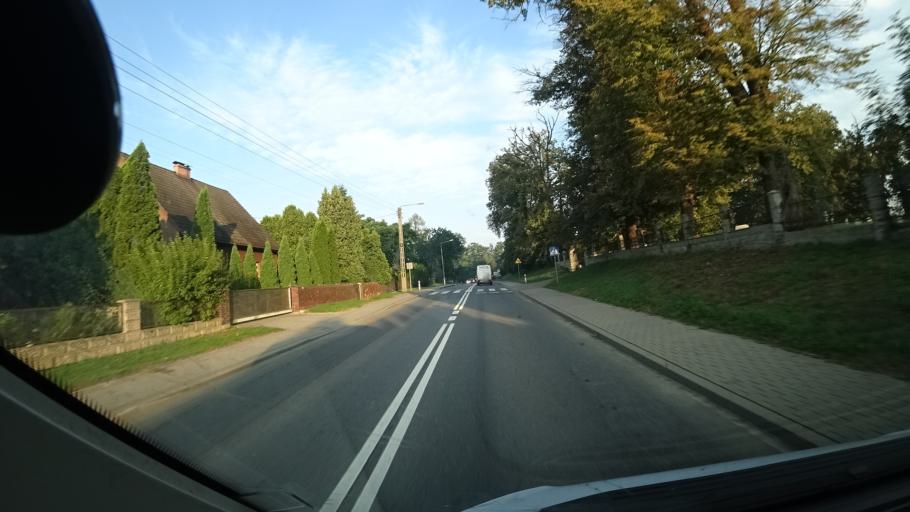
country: PL
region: Opole Voivodeship
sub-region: Powiat strzelecki
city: Ujazd
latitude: 50.3878
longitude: 18.3595
